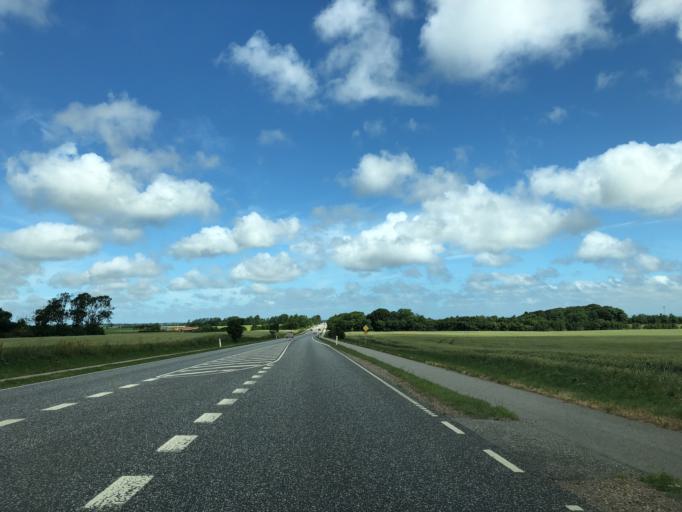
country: DK
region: Central Jutland
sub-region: Struer Kommune
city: Struer
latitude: 56.4299
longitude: 8.5982
